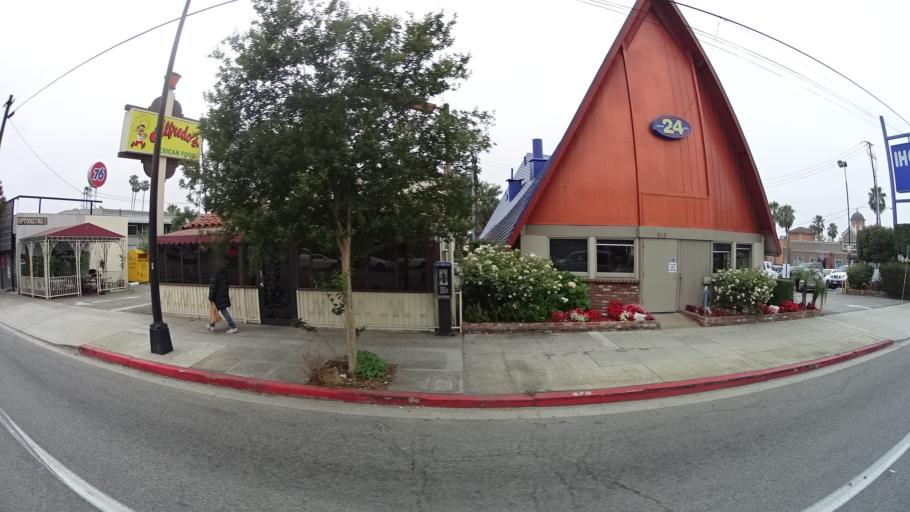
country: US
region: California
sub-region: Los Angeles County
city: Burbank
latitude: 34.1868
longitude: -118.3170
